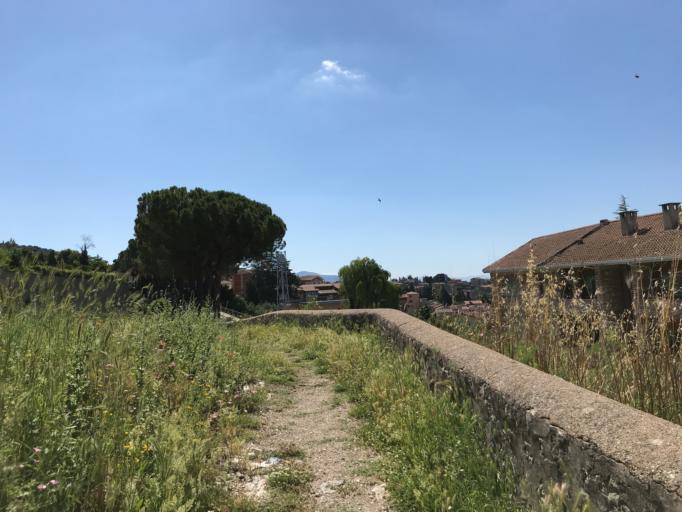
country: IT
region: Umbria
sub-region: Provincia di Terni
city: Amelia
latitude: 42.5546
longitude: 12.4128
